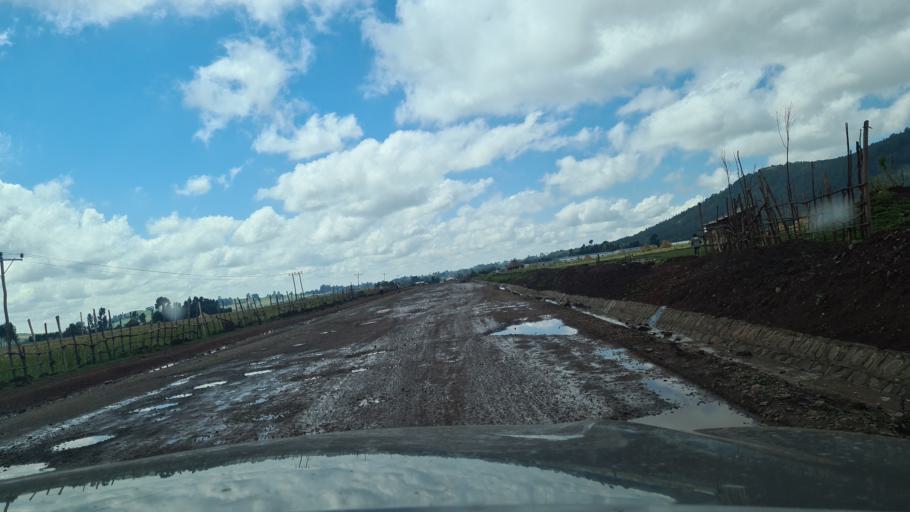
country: ET
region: Oromiya
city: Huruta
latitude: 8.0849
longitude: 39.5417
